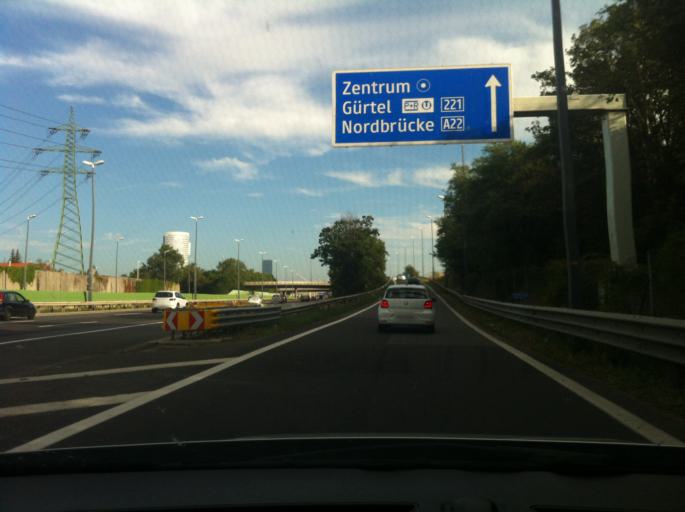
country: AT
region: Lower Austria
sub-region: Politischer Bezirk Korneuburg
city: Langenzersdorf
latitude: 48.2606
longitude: 16.3817
